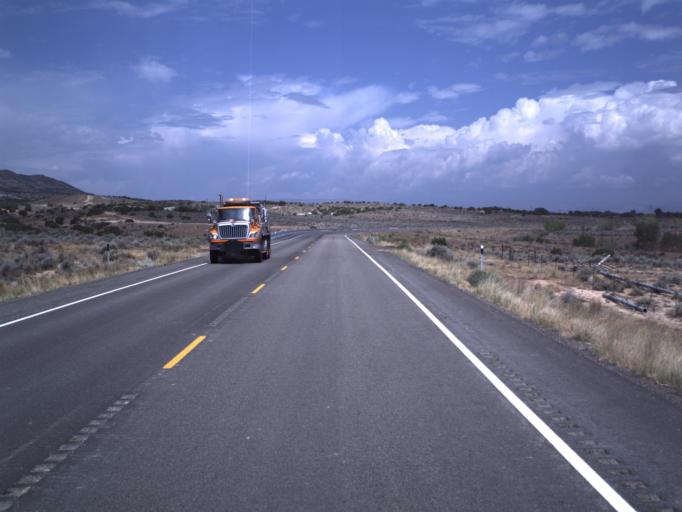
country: US
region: Utah
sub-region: Uintah County
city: Naples
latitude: 40.3541
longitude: -109.4953
